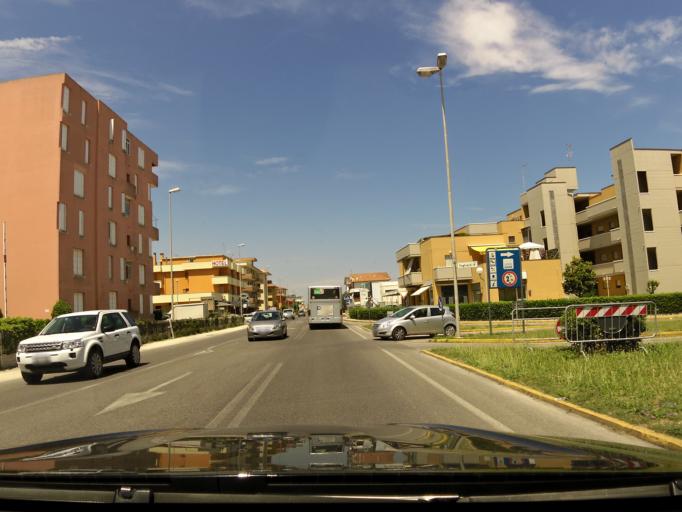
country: IT
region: The Marches
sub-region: Provincia di Pesaro e Urbino
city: Marotta
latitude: 43.7637
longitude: 13.1466
